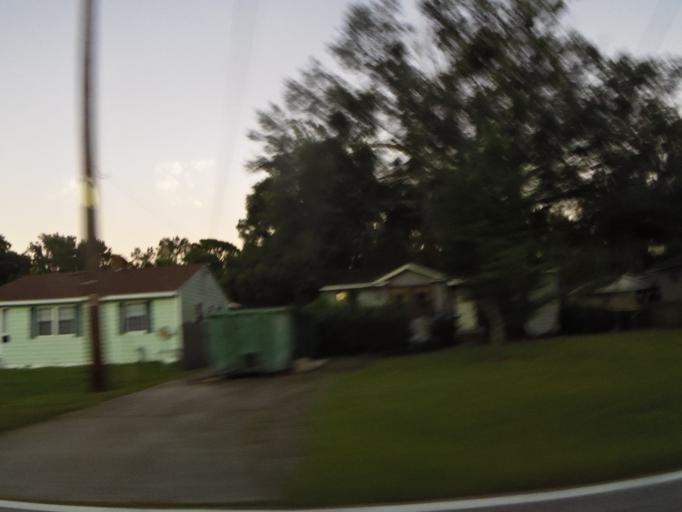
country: US
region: Florida
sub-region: Duval County
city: Jacksonville
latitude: 30.2996
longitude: -81.7220
